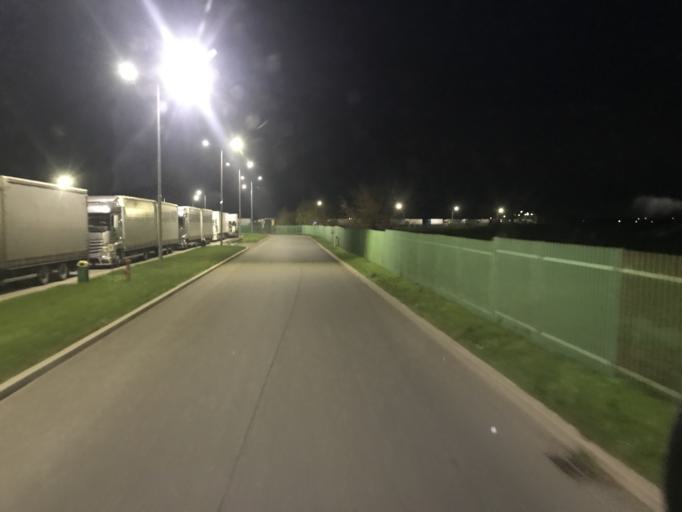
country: PL
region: Lublin Voivodeship
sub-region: Powiat bialski
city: Terespol
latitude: 52.0778
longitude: 23.5225
